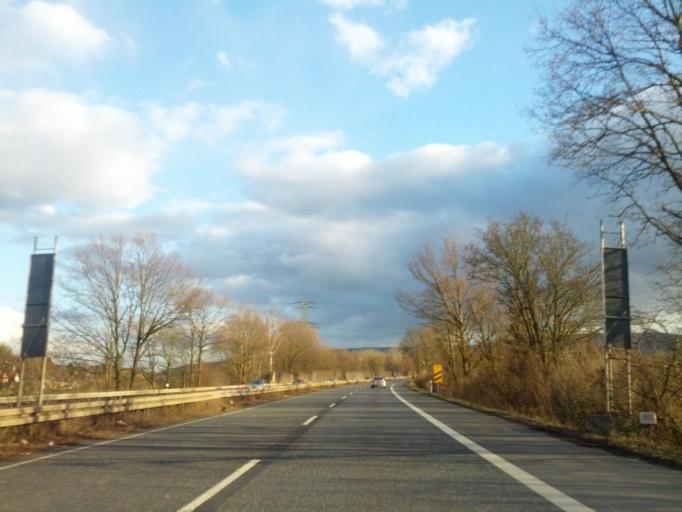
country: DE
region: Hesse
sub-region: Regierungsbezirk Kassel
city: Kaufungen
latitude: 51.2899
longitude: 9.5809
